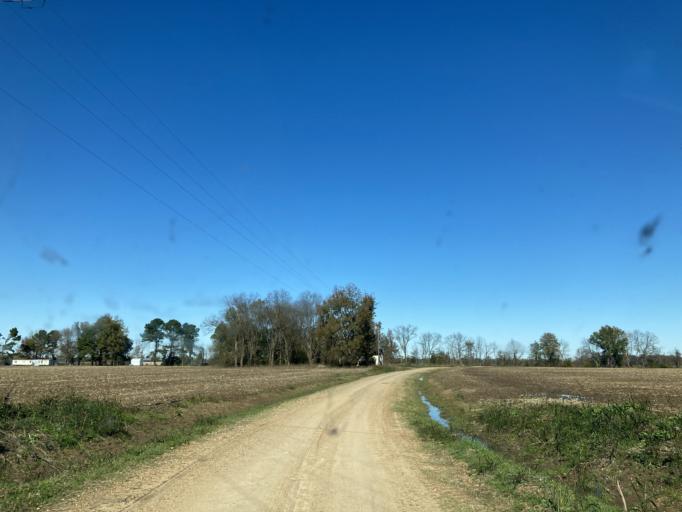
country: US
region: Mississippi
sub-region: Hinds County
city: Lynchburg
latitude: 32.6363
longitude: -90.6135
